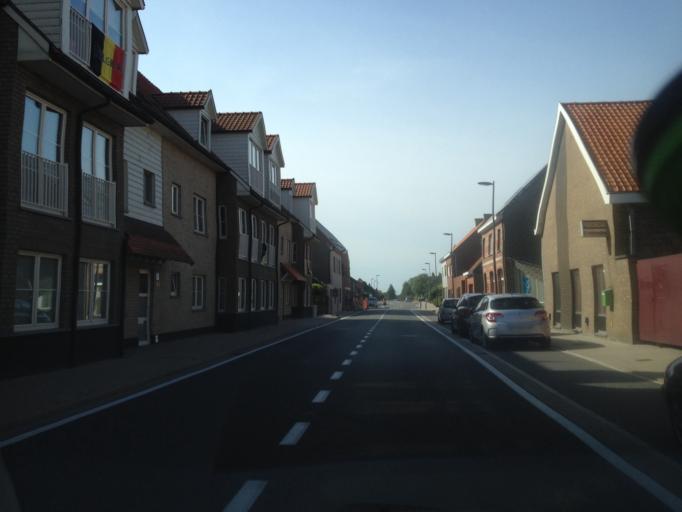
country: BE
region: Flanders
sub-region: Provincie West-Vlaanderen
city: Oudenburg
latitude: 51.1651
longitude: 3.0156
